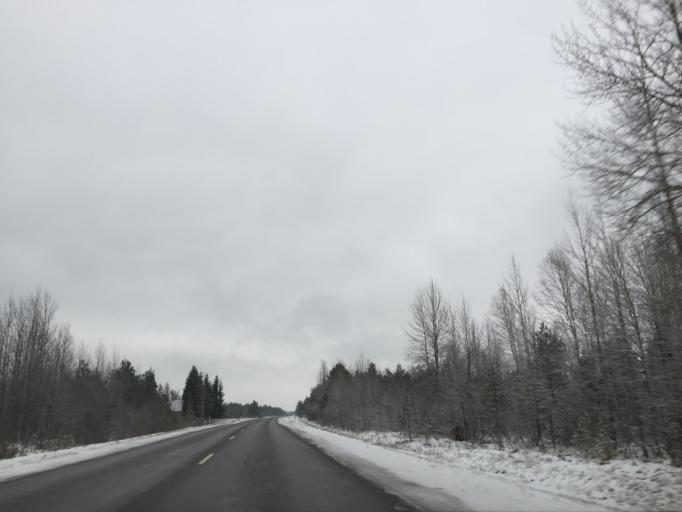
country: EE
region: Laeaene
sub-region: Lihula vald
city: Lihula
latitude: 58.6220
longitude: 23.9010
